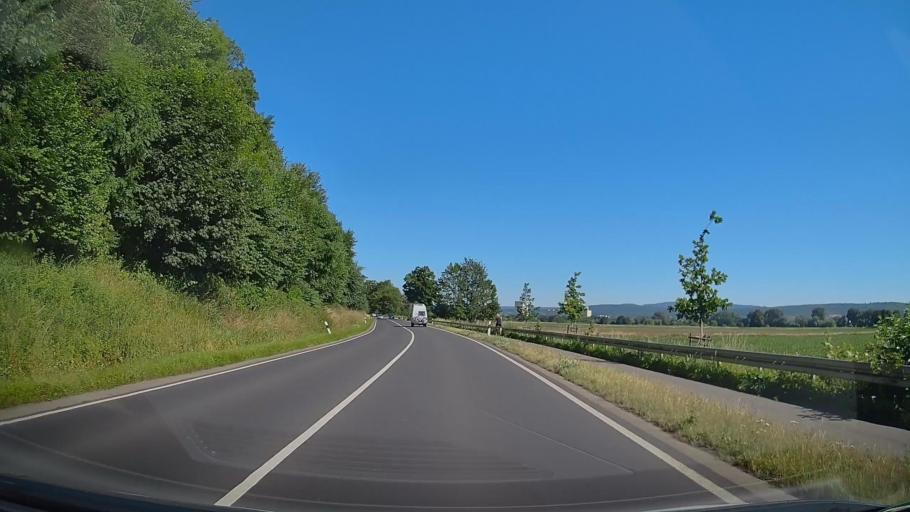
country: DE
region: Lower Saxony
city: Hameln
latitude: 52.0799
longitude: 9.3607
